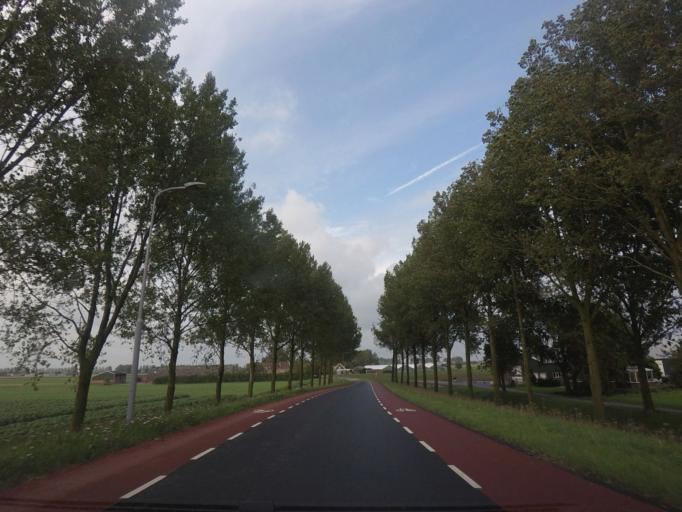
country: NL
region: South Holland
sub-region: Gemeente Kaag en Braassem
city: Oude Wetering
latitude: 52.2454
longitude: 4.6456
